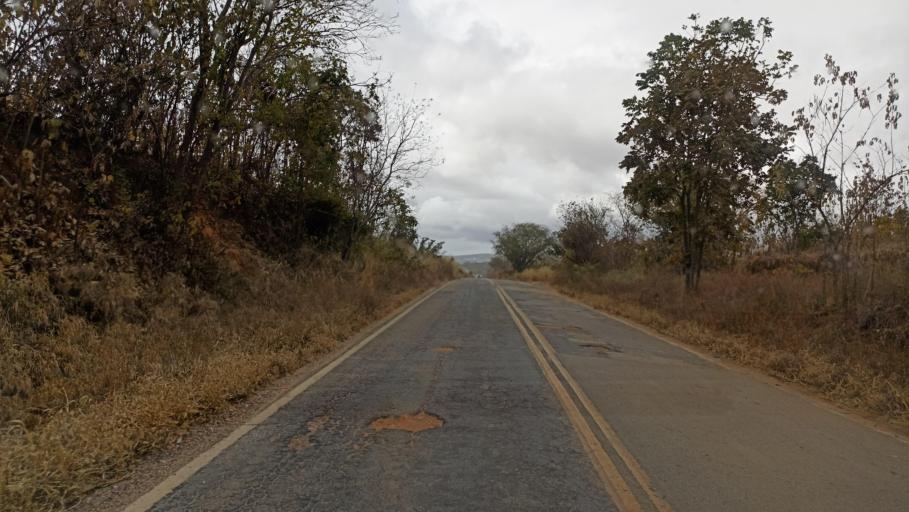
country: BR
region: Minas Gerais
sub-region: Itinga
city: Itinga
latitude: -16.6385
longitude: -41.8114
